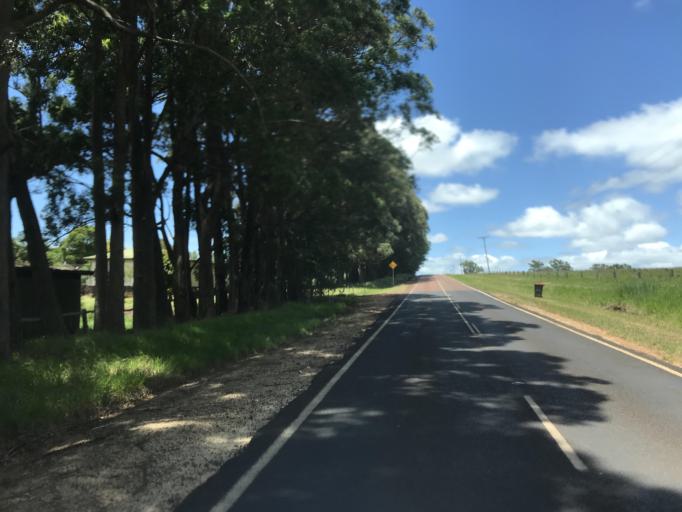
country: AU
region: Queensland
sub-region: Tablelands
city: Ravenshoe
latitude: -17.5319
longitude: 145.4532
